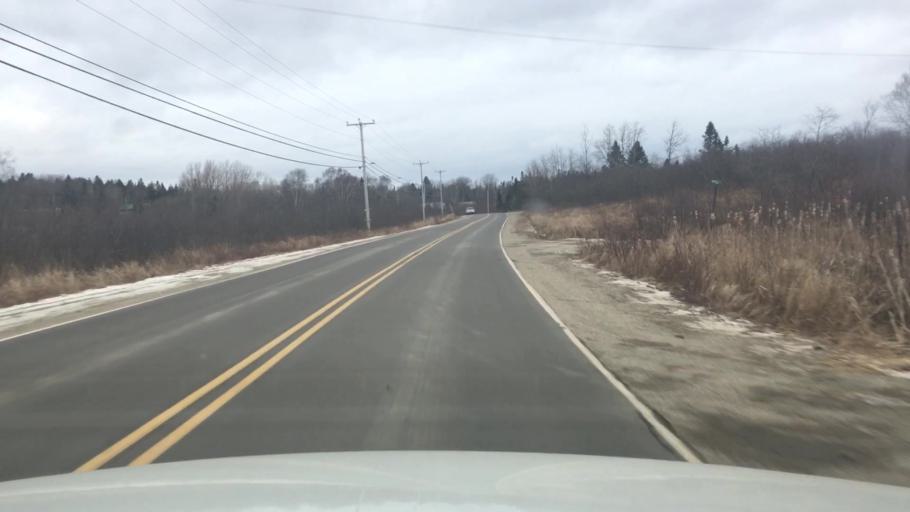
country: US
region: Maine
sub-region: Washington County
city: Jonesport
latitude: 44.5547
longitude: -67.6257
